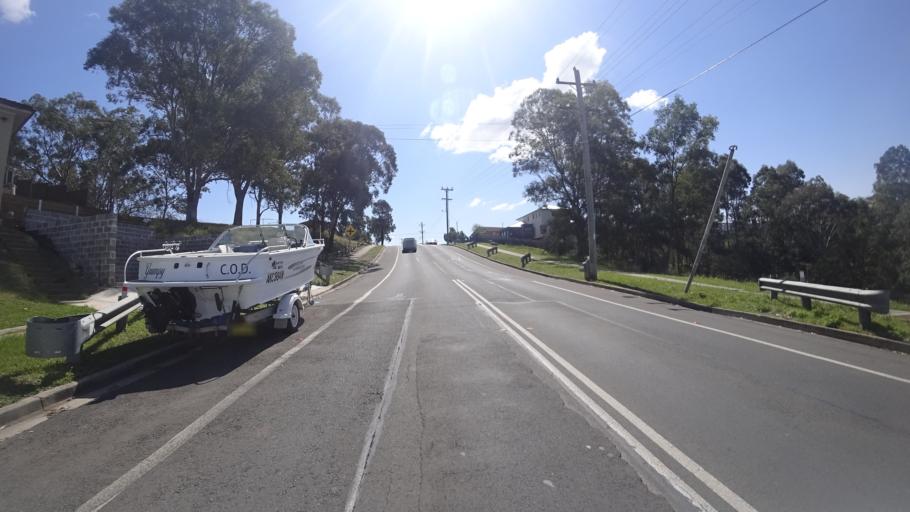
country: AU
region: New South Wales
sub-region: Liverpool
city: Miller
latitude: -33.9109
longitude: 150.8941
